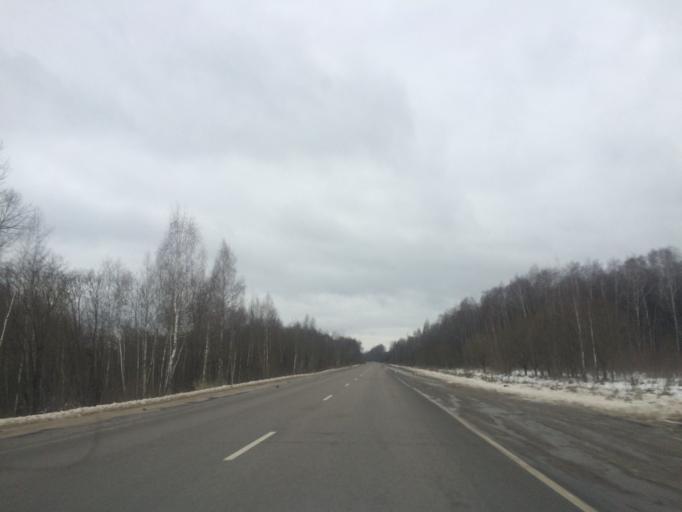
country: RU
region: Tula
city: Pervomayskiy
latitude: 54.1327
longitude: 37.3460
